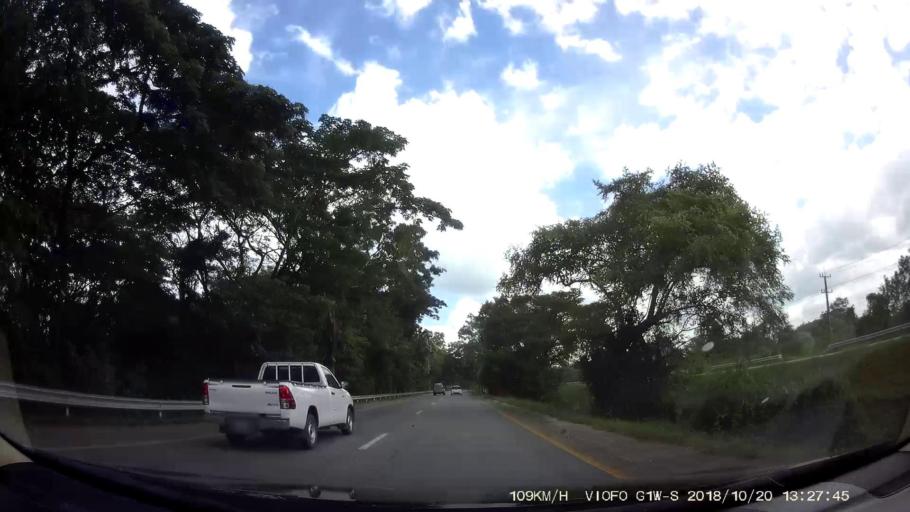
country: TH
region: Chaiyaphum
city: Khon San
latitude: 16.5922
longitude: 101.9653
